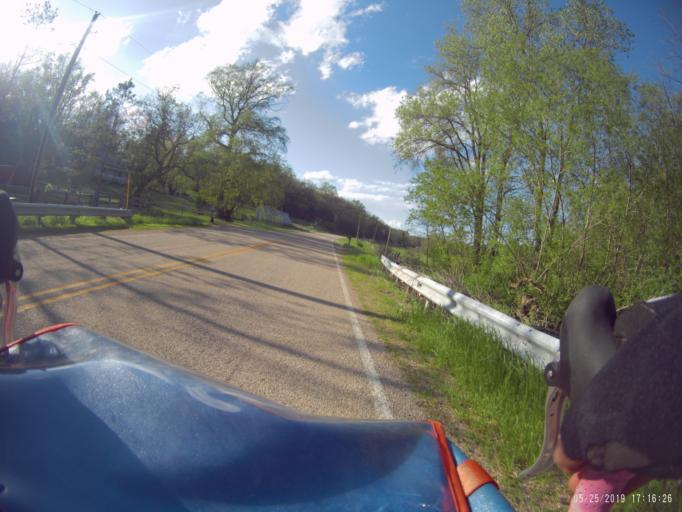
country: US
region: Wisconsin
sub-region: Dane County
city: Mount Horeb
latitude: 42.9698
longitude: -89.7896
